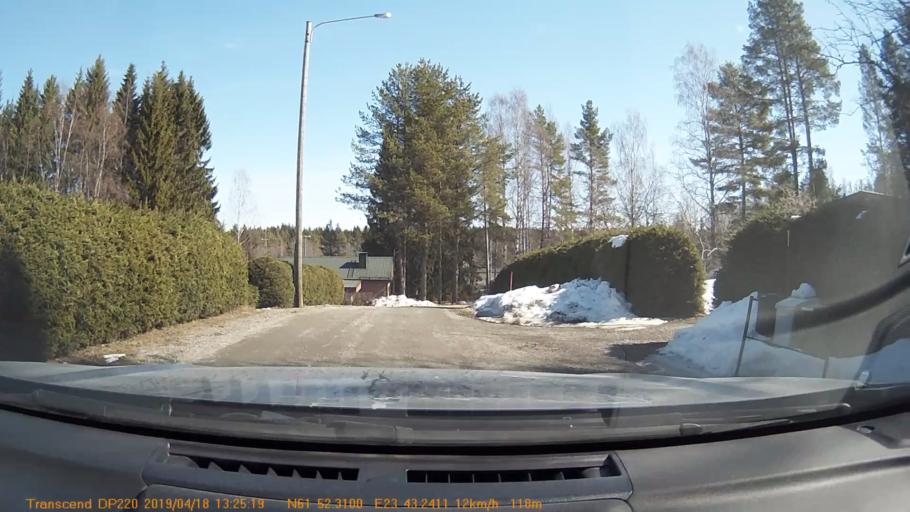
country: FI
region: Pirkanmaa
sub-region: Tampere
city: Kuru
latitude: 61.8718
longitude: 23.7206
